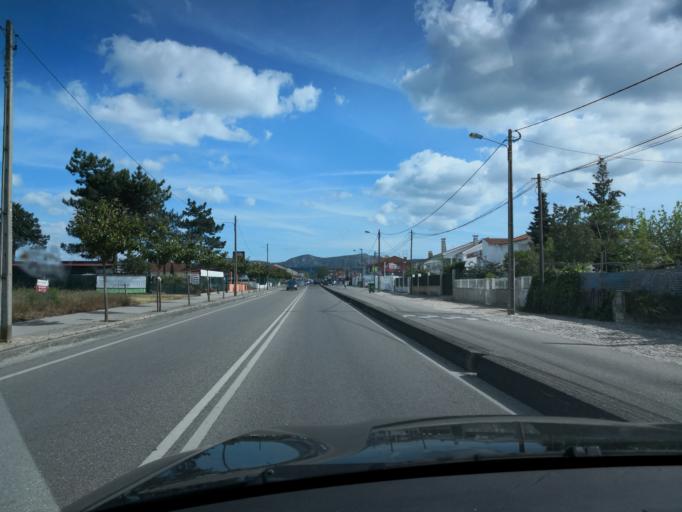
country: PT
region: Setubal
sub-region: Barreiro
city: Santo Antonio da Charneca
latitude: 38.5417
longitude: -9.0273
